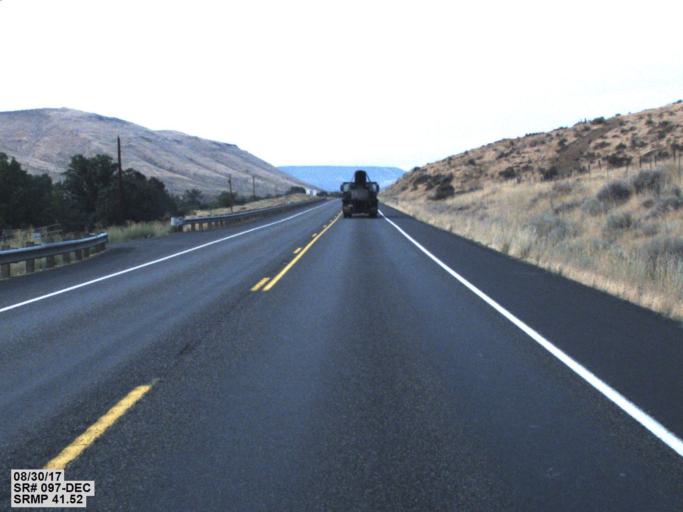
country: US
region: Washington
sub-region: Yakima County
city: Toppenish
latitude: 46.1472
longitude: -120.5129
